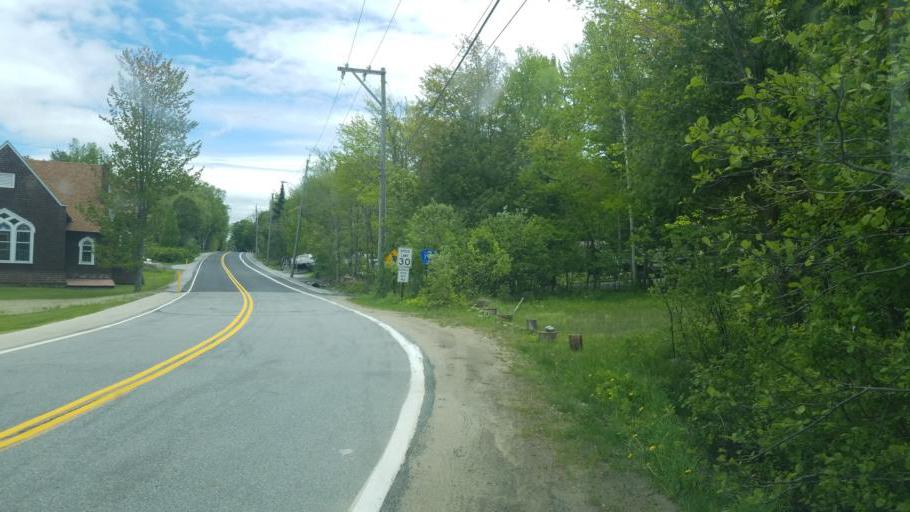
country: US
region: New York
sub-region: Franklin County
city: Tupper Lake
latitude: 43.8542
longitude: -74.4385
